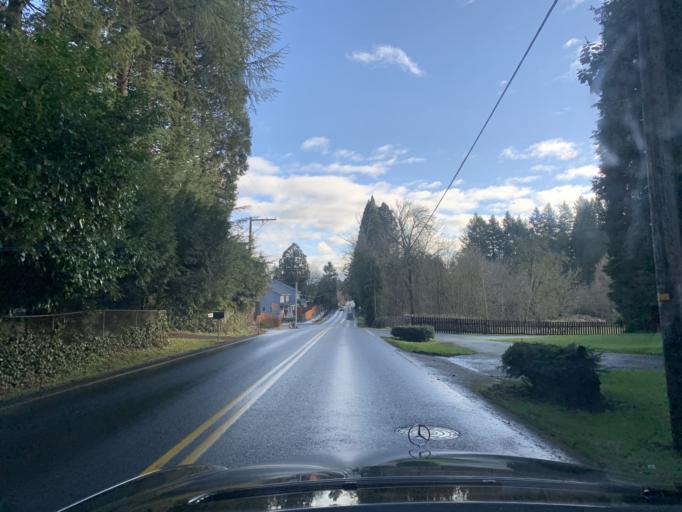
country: US
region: Washington
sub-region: Clark County
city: Barberton
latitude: 45.6861
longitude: -122.5897
